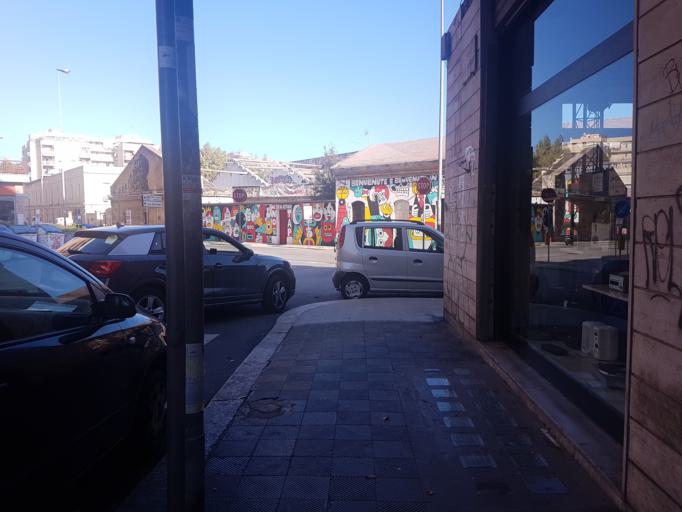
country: IT
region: Apulia
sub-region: Provincia di Bari
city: Bari
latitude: 41.1148
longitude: 16.8685
